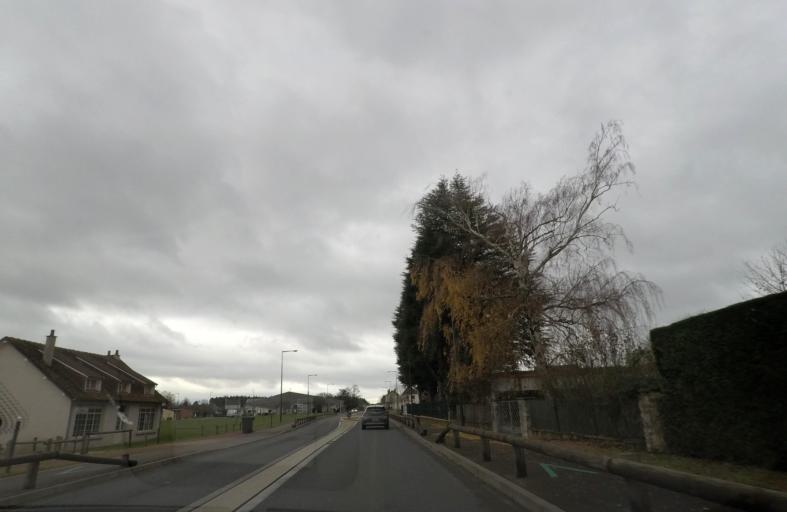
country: FR
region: Centre
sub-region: Departement du Loir-et-Cher
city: Cour-Cheverny
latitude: 47.5135
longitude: 1.4548
